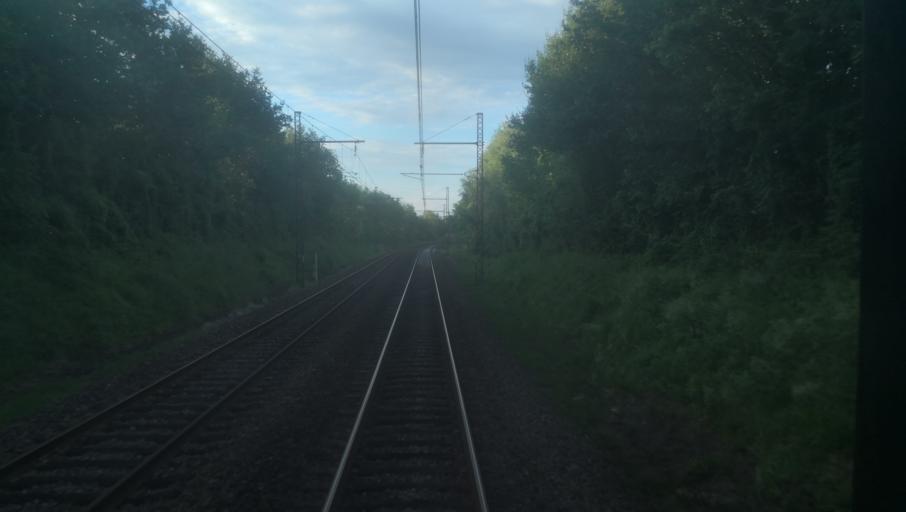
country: FR
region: Centre
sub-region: Departement de l'Indre
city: Le Pechereau
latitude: 46.5376
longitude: 1.5371
